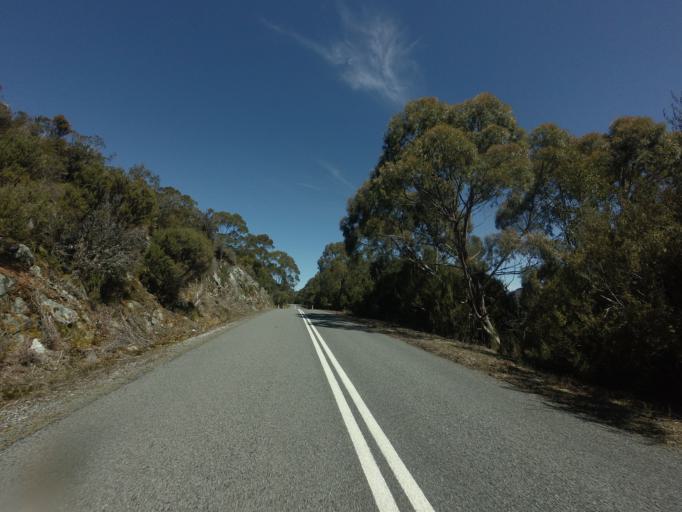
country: AU
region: Tasmania
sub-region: Huon Valley
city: Geeveston
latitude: -42.8243
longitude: 146.1250
